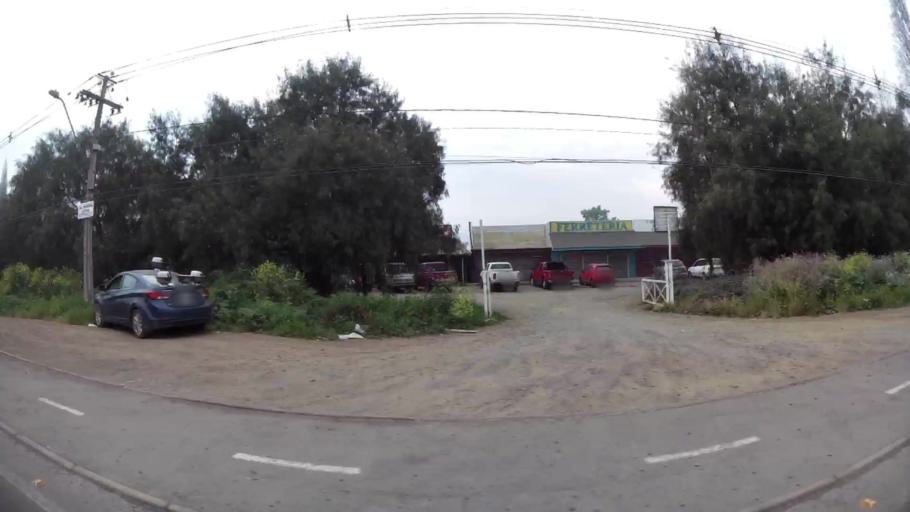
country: CL
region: Santiago Metropolitan
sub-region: Provincia de Chacabuco
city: Lampa
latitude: -33.2318
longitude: -70.7713
